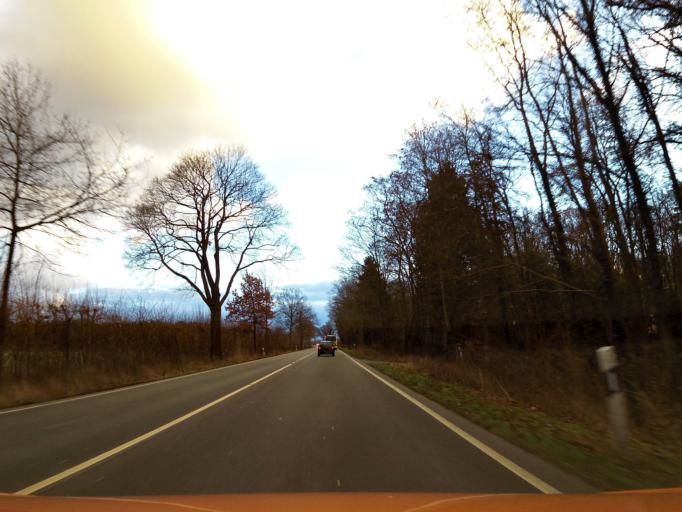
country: DE
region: Lower Saxony
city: Didderse
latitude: 52.3646
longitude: 10.3915
